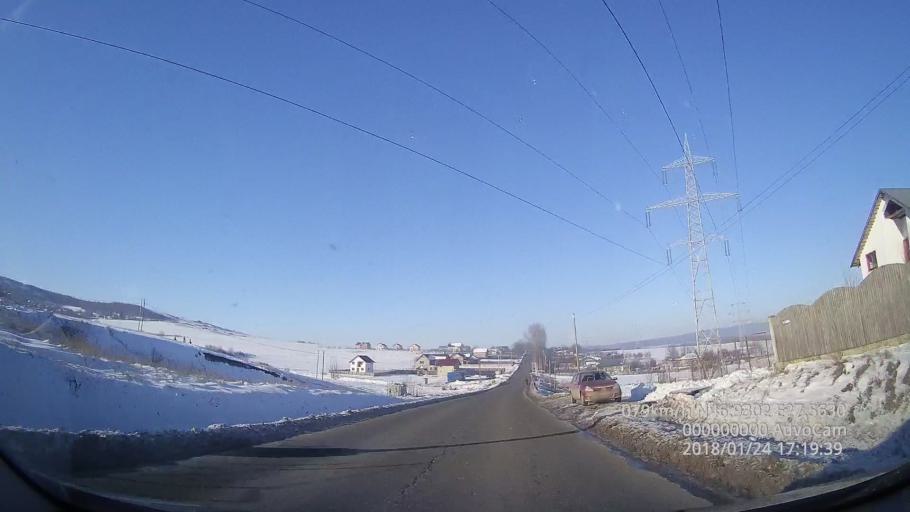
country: RO
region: Iasi
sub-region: Comuna Scanteia
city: Scanteia
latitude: 46.9308
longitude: 27.5629
